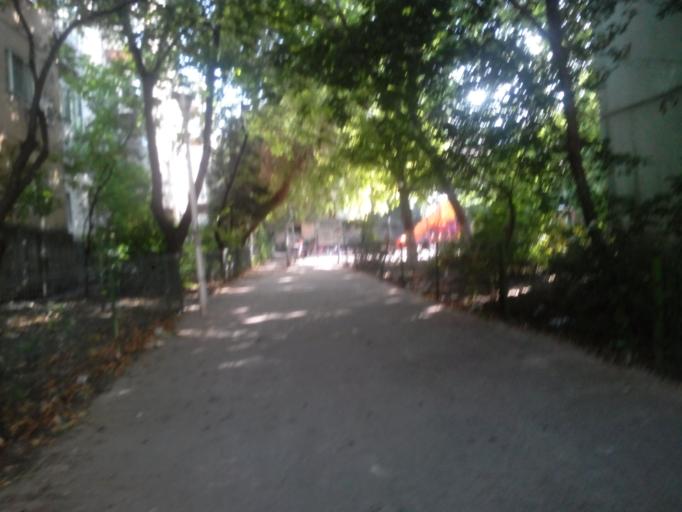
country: RO
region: Ilfov
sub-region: Comuna Chiajna
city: Rosu
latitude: 44.4386
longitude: 26.0198
